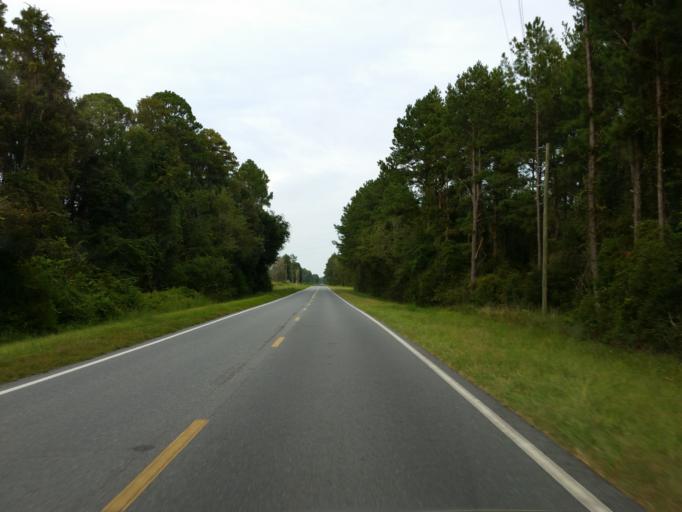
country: US
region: Georgia
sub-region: Echols County
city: Statenville
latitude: 30.5743
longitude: -83.1485
